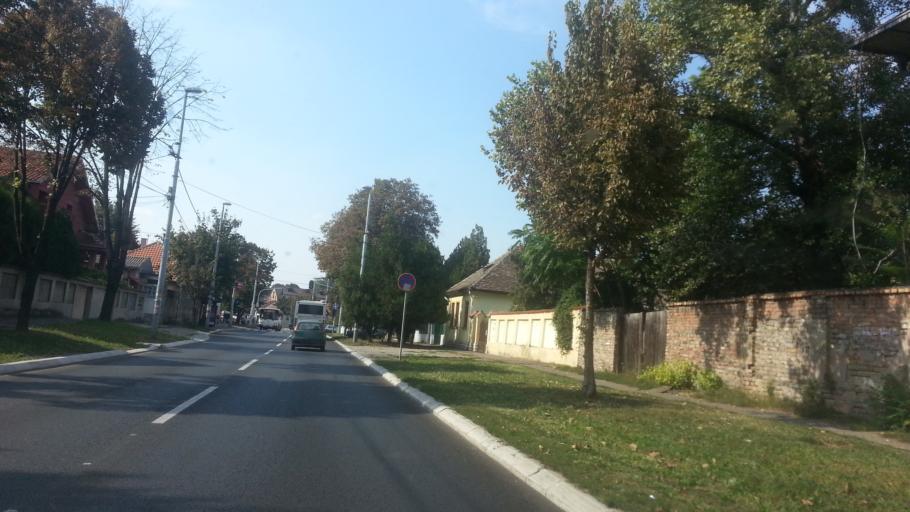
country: RS
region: Central Serbia
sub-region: Belgrade
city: Zemun
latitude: 44.8488
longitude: 20.3930
